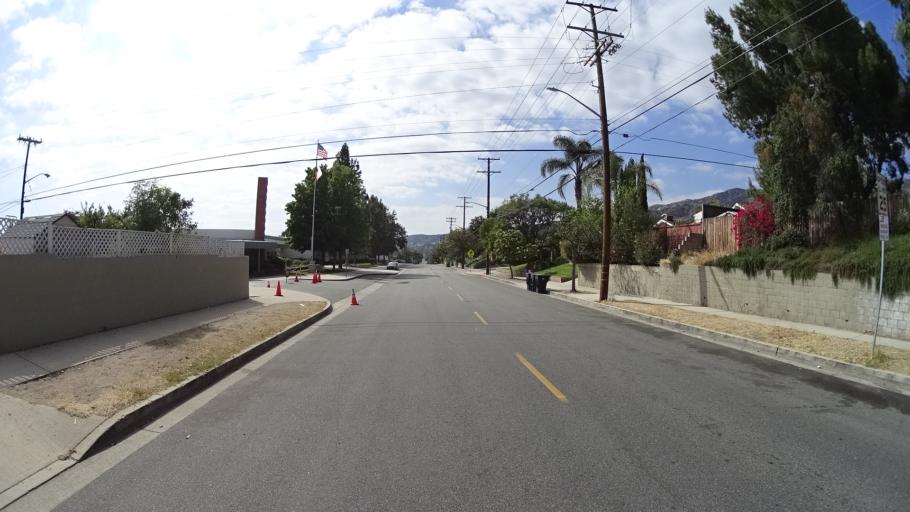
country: US
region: California
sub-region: Los Angeles County
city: Burbank
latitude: 34.1945
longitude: -118.3106
